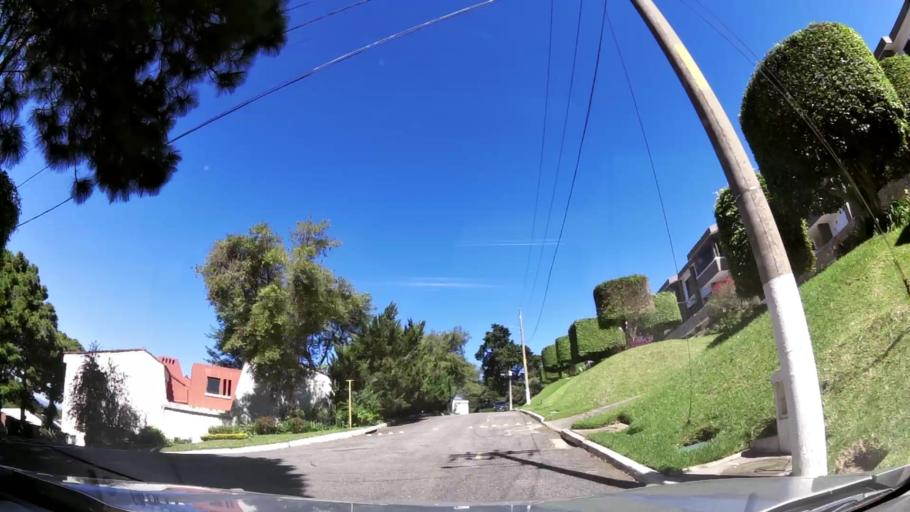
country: GT
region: Guatemala
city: San Jose Pinula
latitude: 14.5422
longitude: -90.4559
